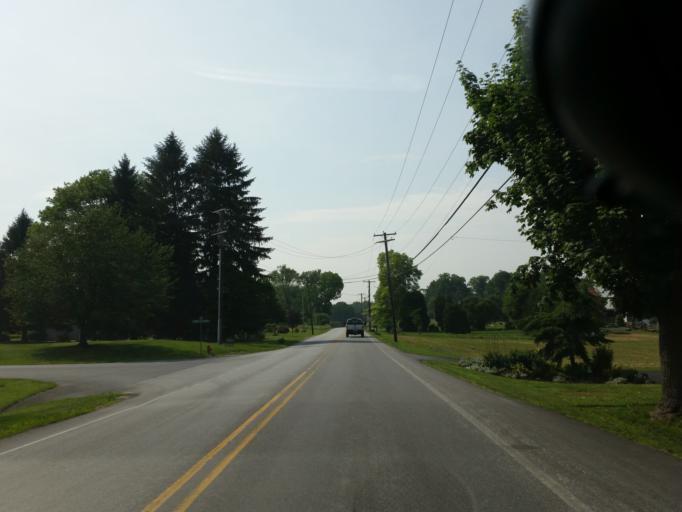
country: US
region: Pennsylvania
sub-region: Lancaster County
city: Lampeter
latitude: 40.0175
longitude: -76.2344
